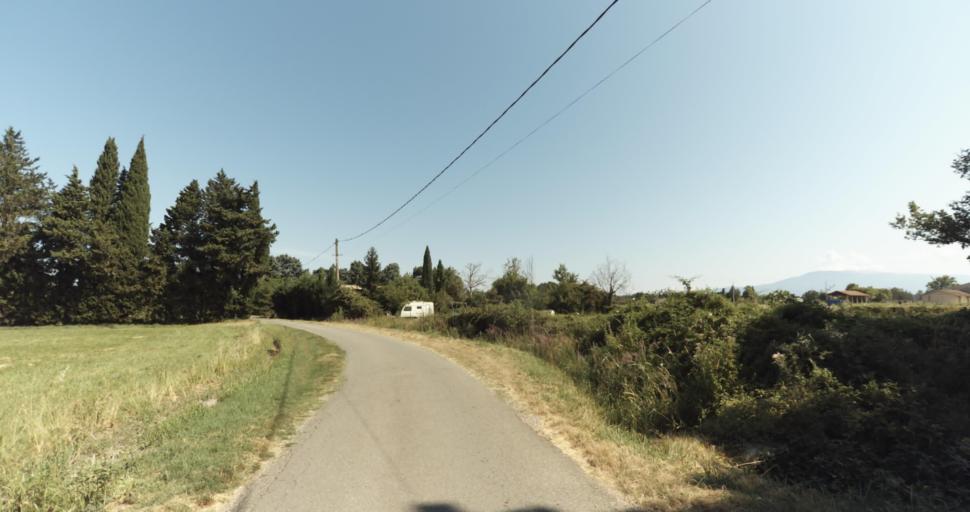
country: FR
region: Provence-Alpes-Cote d'Azur
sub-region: Departement du Vaucluse
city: Monteux
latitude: 44.0129
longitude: 5.0026
